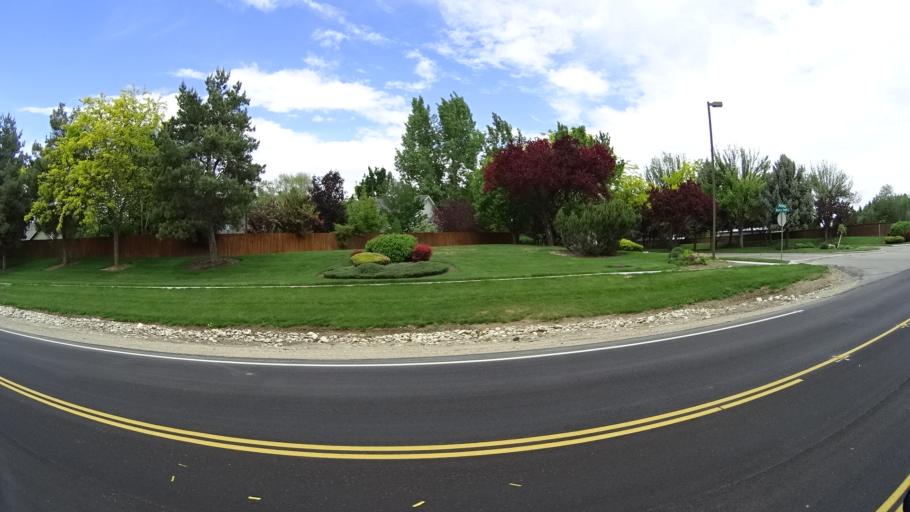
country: US
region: Idaho
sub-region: Ada County
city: Meridian
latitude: 43.5757
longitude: -116.3602
